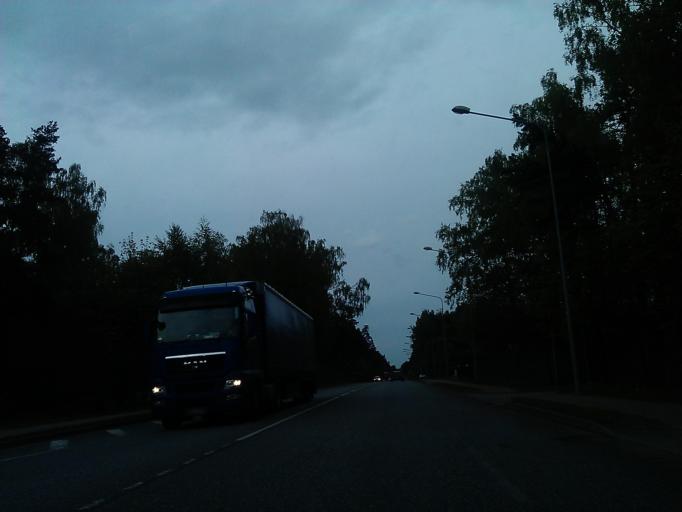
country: LV
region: Adazi
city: Adazi
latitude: 57.0456
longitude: 24.3165
